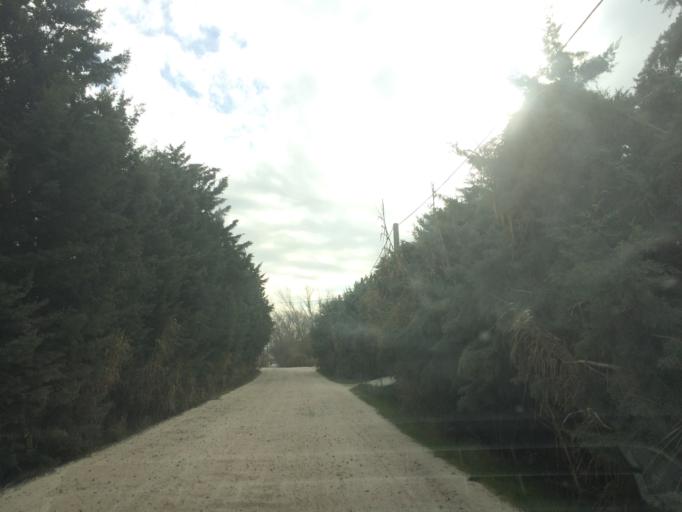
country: ES
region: Madrid
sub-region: Provincia de Madrid
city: Arroyomolinos
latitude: 40.3121
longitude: -3.9472
